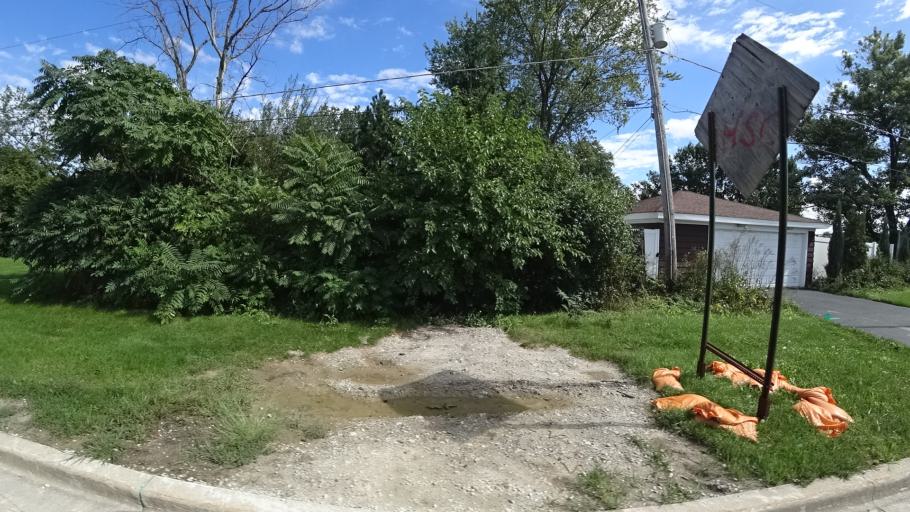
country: US
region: Illinois
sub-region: Cook County
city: Oak Lawn
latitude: 41.7221
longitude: -87.7663
